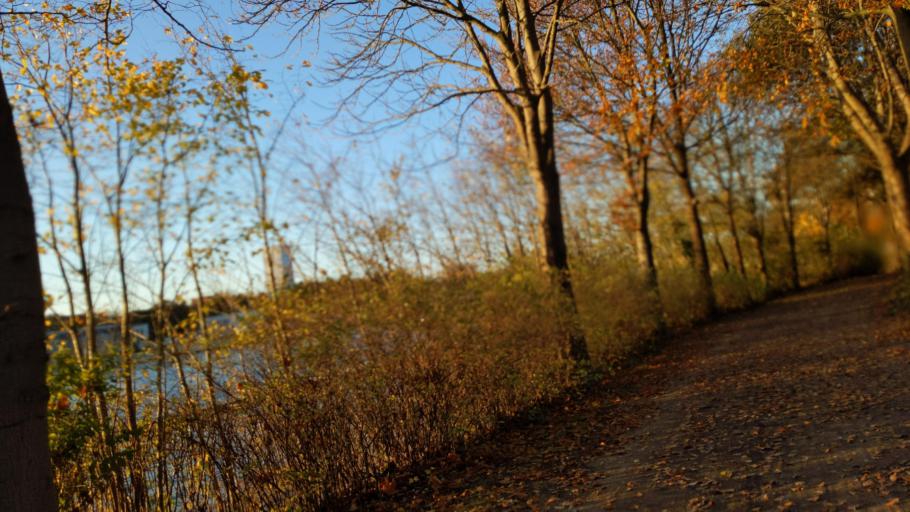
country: DE
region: Schleswig-Holstein
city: Neustadt in Holstein
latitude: 54.0980
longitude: 10.8151
